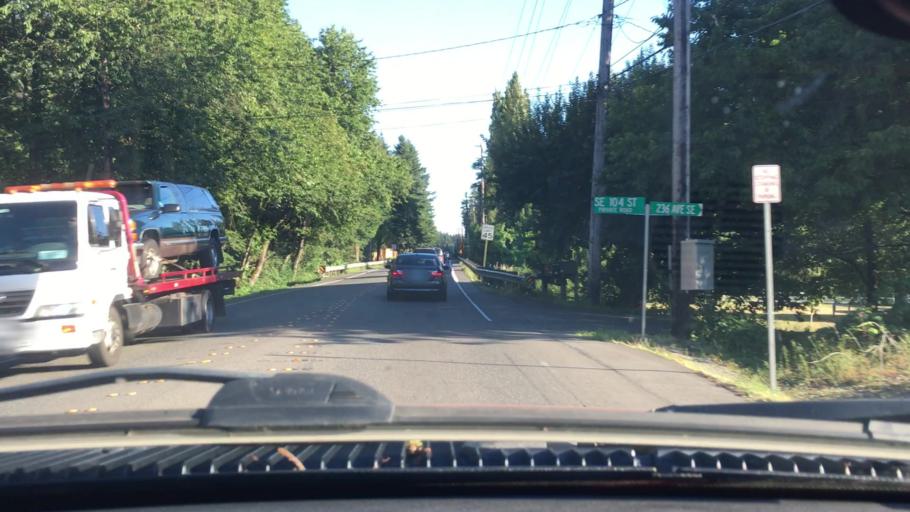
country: US
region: Washington
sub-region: King County
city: Issaquah
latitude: 47.5092
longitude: -122.0231
